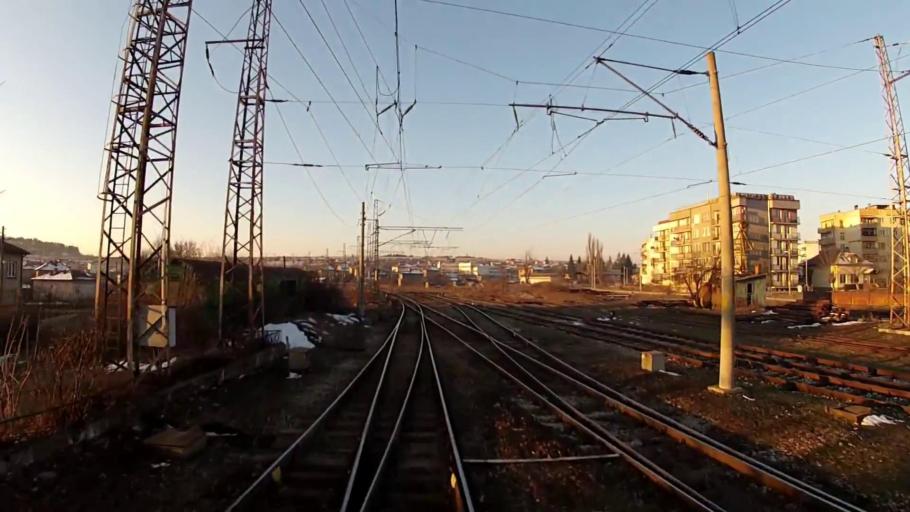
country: BG
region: Sofiya
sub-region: Obshtina Dragoman
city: Dragoman
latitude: 42.9173
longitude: 22.9316
